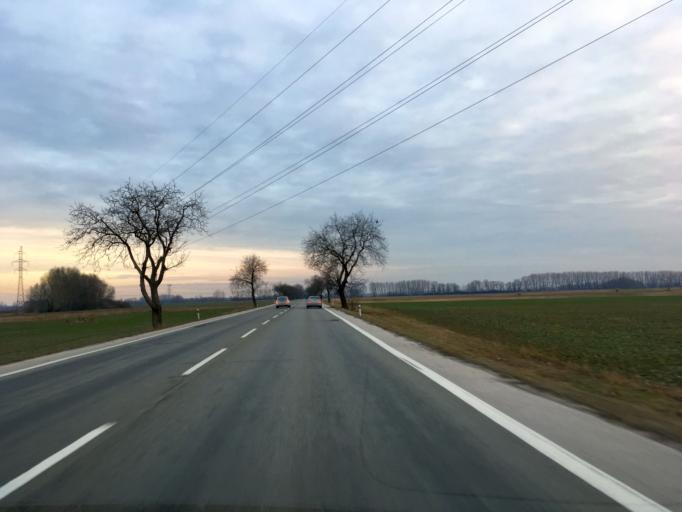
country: SK
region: Trnavsky
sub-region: Okres Dunajska Streda
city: Velky Meder
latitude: 47.8957
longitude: 17.7416
